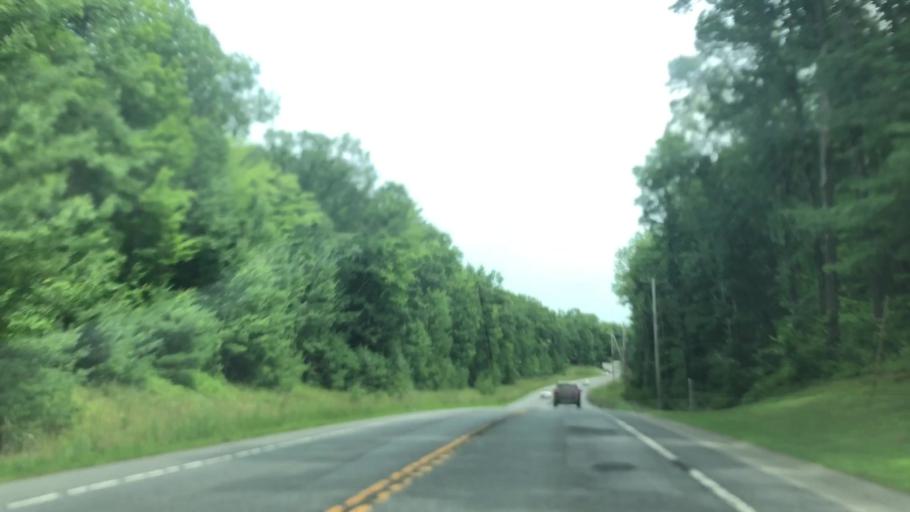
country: US
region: New York
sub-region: Warren County
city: Glens Falls North
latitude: 43.3720
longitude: -73.6867
